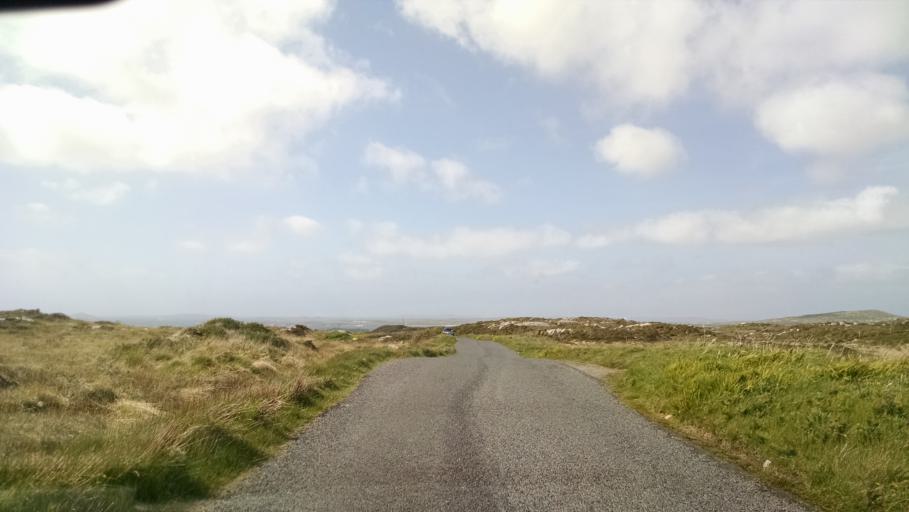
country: IE
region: Connaught
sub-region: County Galway
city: Clifden
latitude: 53.5049
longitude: -10.1055
